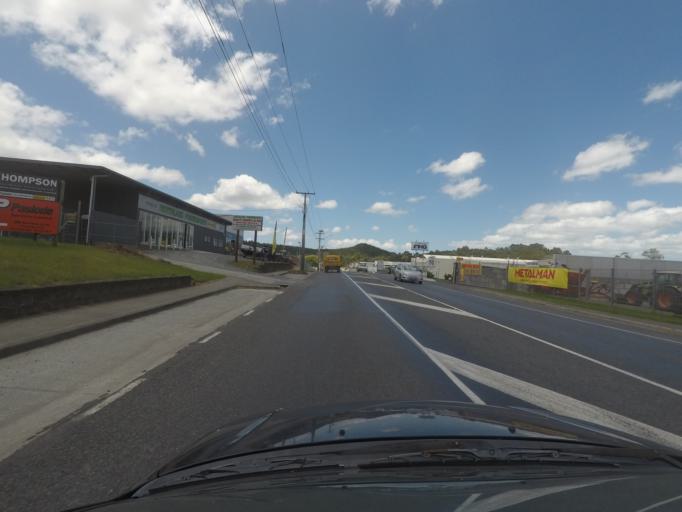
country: NZ
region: Northland
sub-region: Whangarei
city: Whangarei
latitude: -35.7522
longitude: 174.3134
